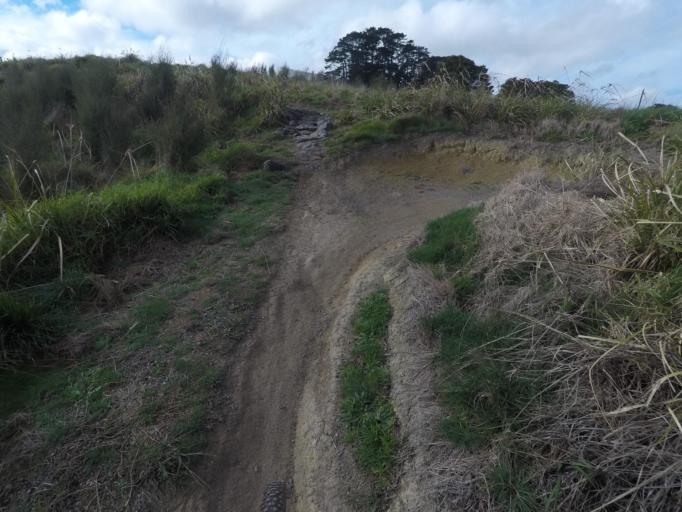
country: NZ
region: Auckland
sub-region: Auckland
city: Manukau City
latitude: -36.9953
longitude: 174.9123
